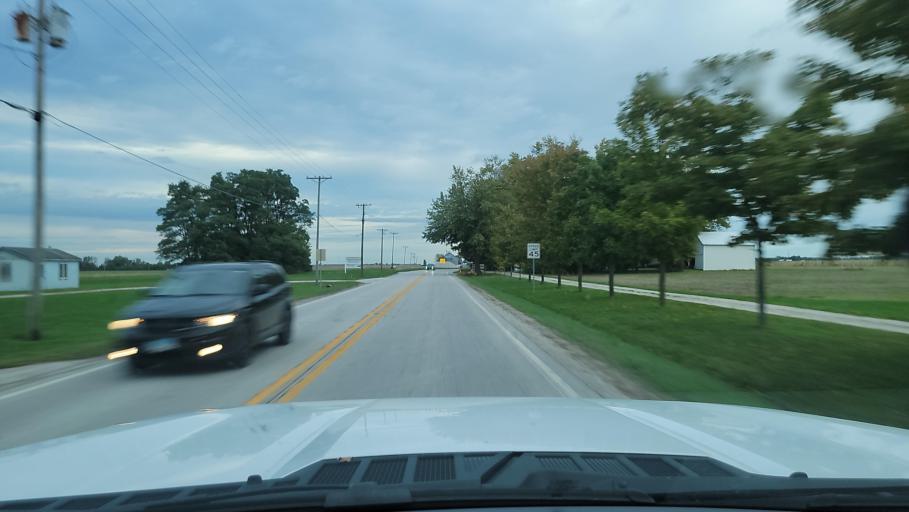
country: US
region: Illinois
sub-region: Schuyler County
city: Rushville
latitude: 40.1333
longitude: -90.5623
